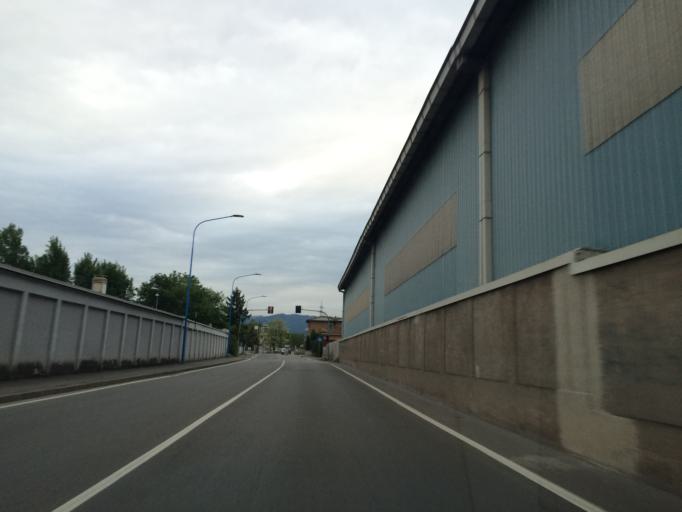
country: IT
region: Lombardy
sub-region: Provincia di Brescia
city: Folzano
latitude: 45.4948
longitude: 10.2113
